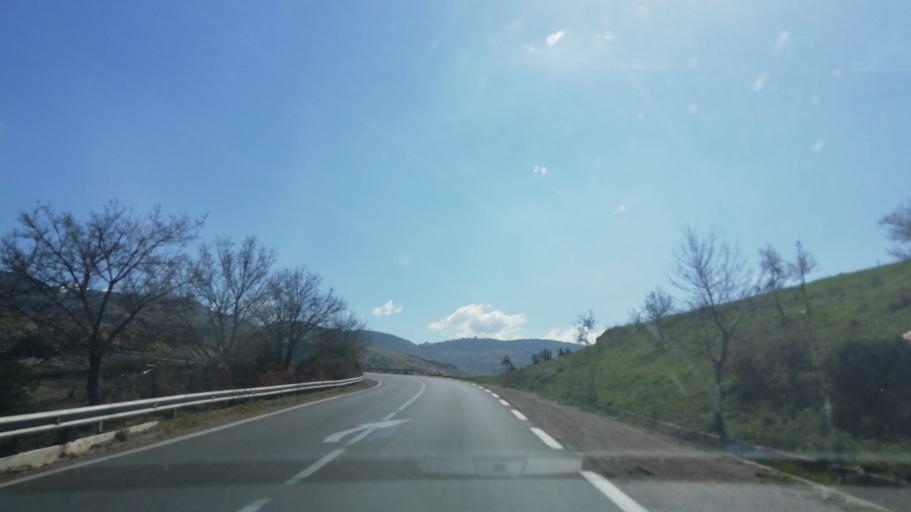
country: DZ
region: Mascara
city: Mascara
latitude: 35.4906
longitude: 0.1371
